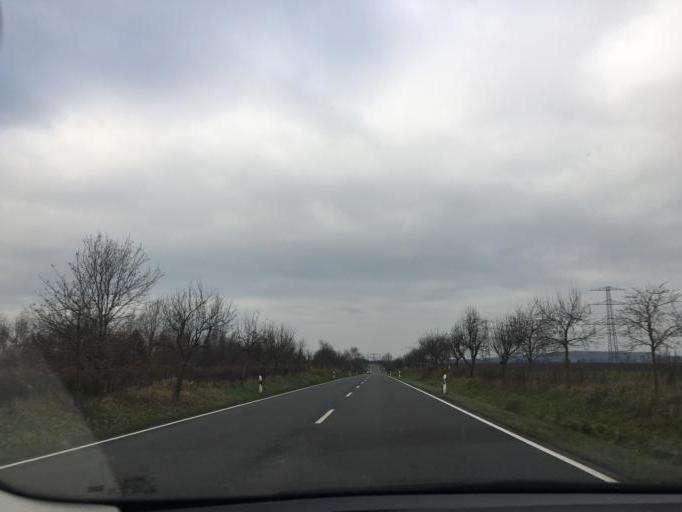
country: DE
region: Saxony
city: Kitzscher
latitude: 51.1375
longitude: 12.5492
